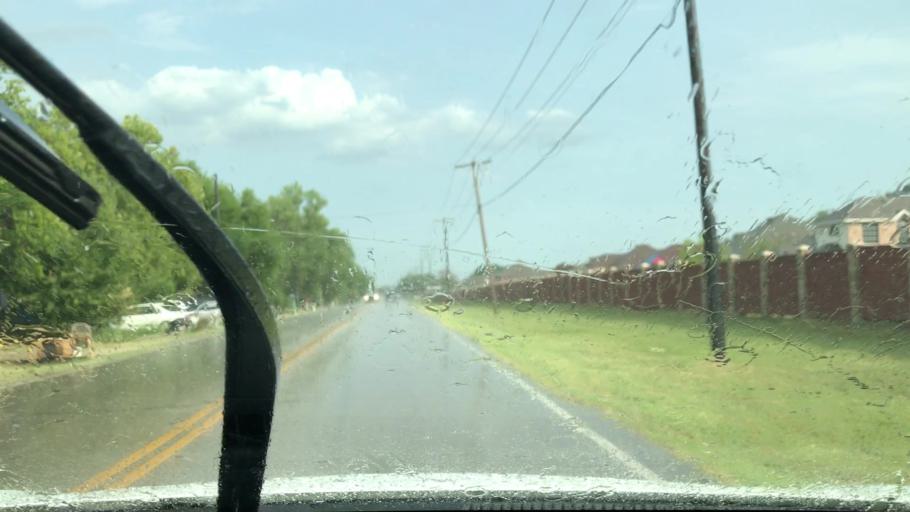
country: US
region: Texas
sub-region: Collin County
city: Wylie
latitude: 32.9602
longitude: -96.5311
